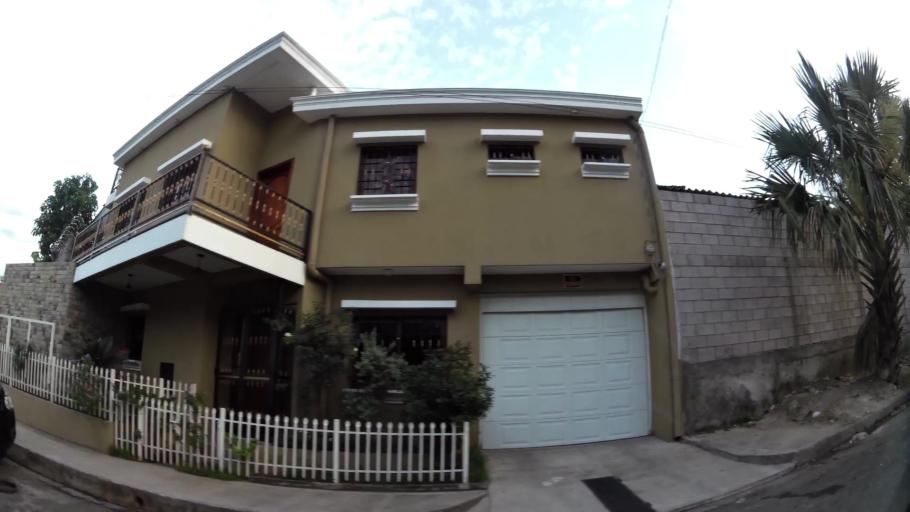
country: SV
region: San Vicente
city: San Vicente
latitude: 13.6459
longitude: -88.7885
